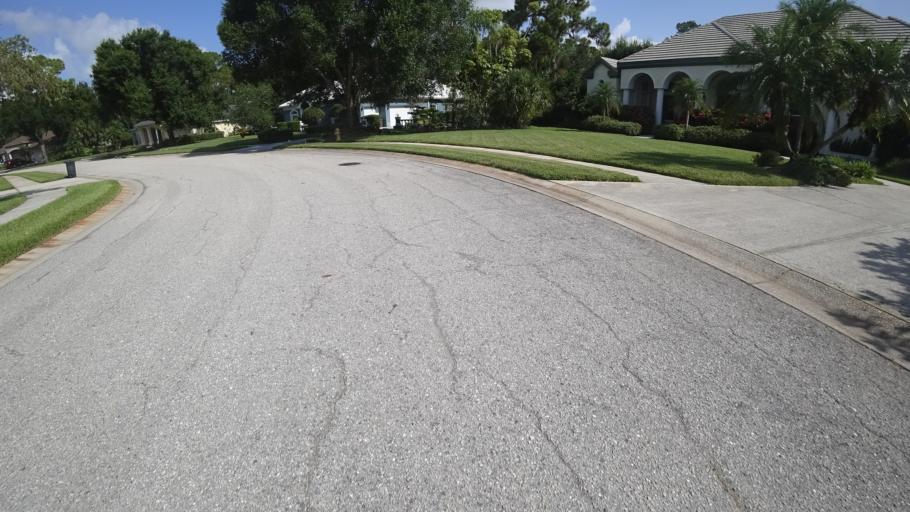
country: US
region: Florida
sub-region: Sarasota County
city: The Meadows
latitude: 27.4048
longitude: -82.4332
